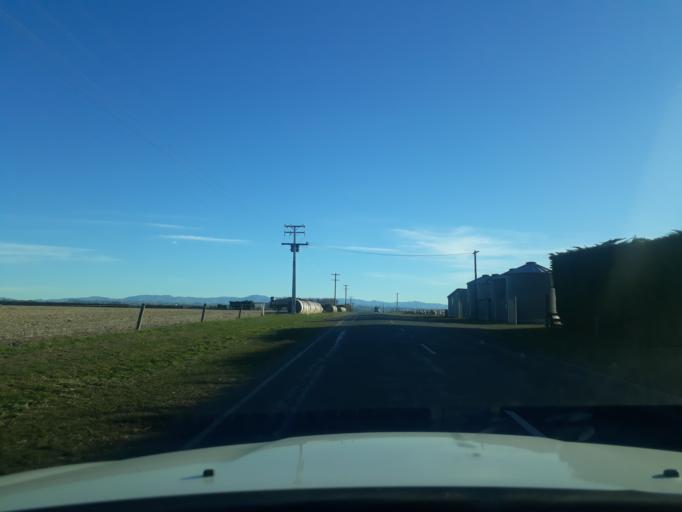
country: NZ
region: Canterbury
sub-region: Timaru District
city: Timaru
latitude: -44.3362
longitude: 171.2216
